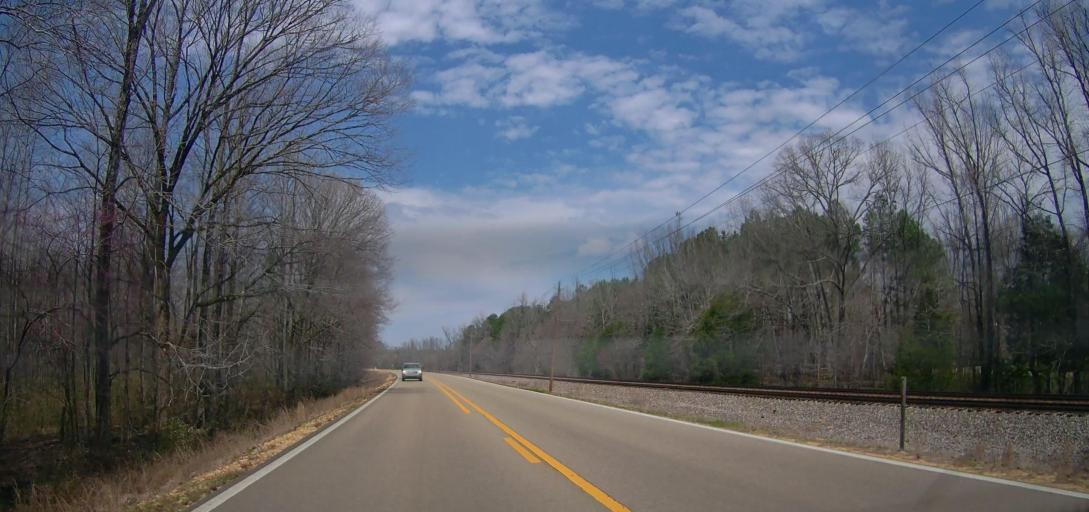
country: US
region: Mississippi
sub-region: Union County
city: New Albany
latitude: 34.5957
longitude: -89.1368
